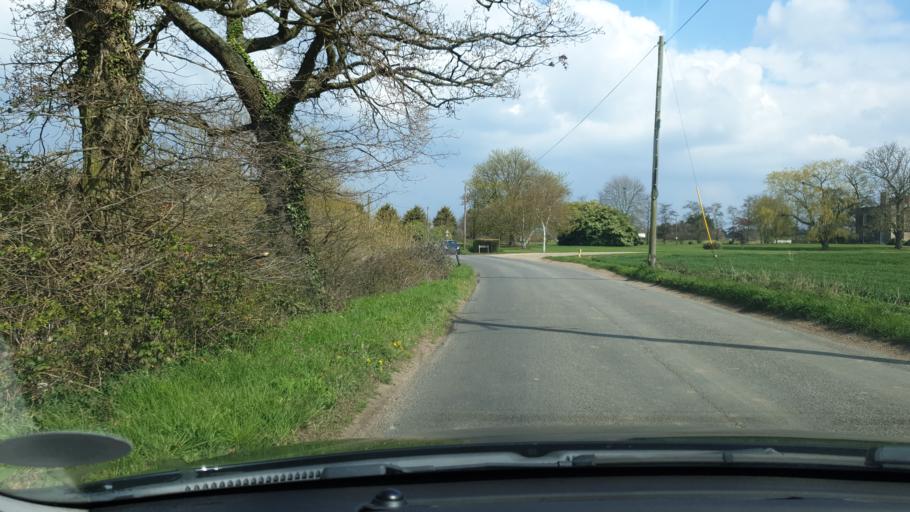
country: GB
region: England
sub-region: Essex
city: Great Bentley
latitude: 51.8663
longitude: 1.1010
